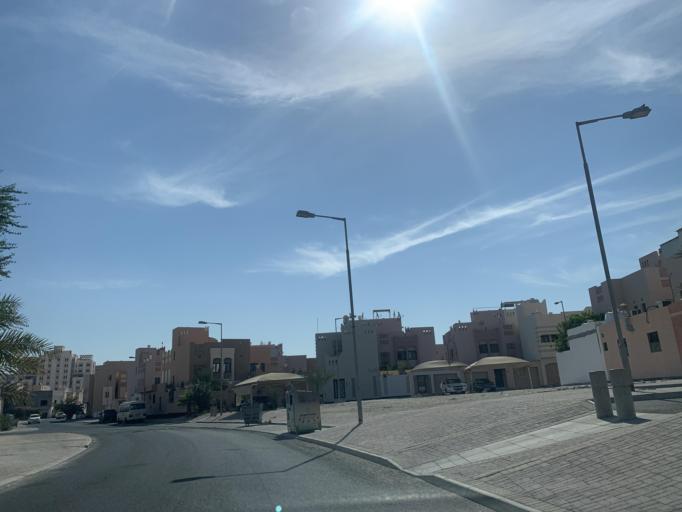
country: BH
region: Central Governorate
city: Madinat Hamad
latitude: 26.1182
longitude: 50.4861
